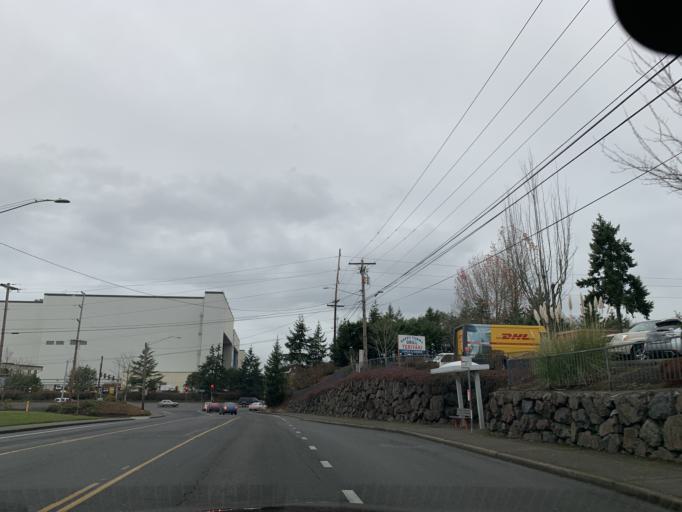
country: US
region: Washington
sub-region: Snohomish County
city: Mukilteo
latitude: 47.9202
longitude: -122.2699
